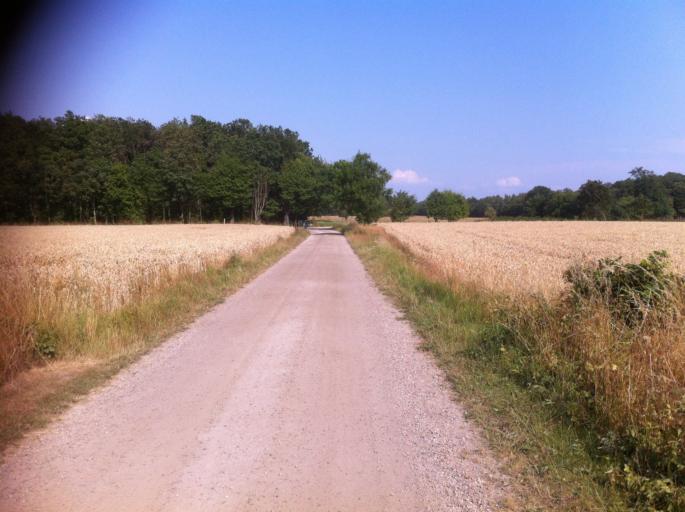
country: SE
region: Skane
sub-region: Lunds Kommun
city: Genarp
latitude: 55.6918
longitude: 13.3275
